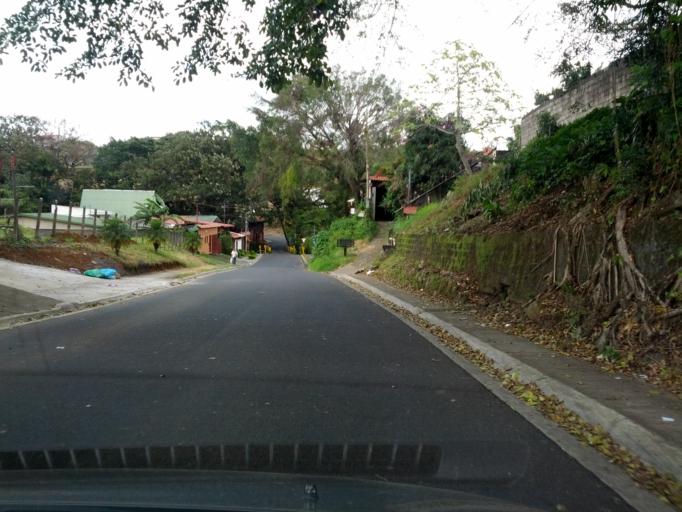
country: CR
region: Alajuela
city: Alajuela
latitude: 10.0243
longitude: -84.2144
